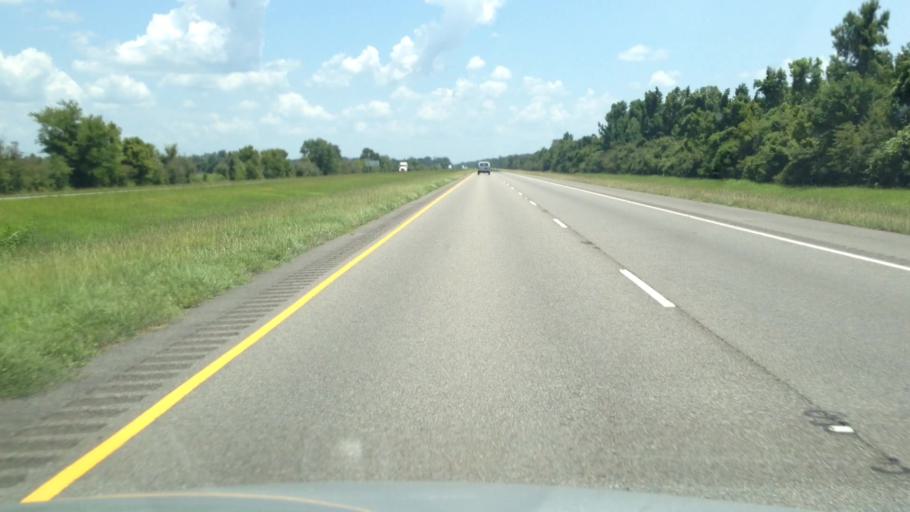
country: US
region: Louisiana
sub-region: Avoyelles Parish
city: Bunkie
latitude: 30.9406
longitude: -92.2667
